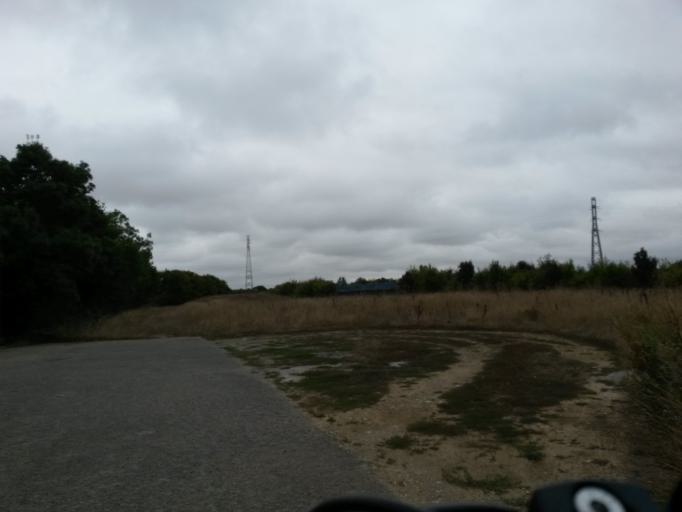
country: FR
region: Poitou-Charentes
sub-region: Departement de la Charente-Maritime
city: Saint-Xandre
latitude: 46.2052
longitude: -1.0911
